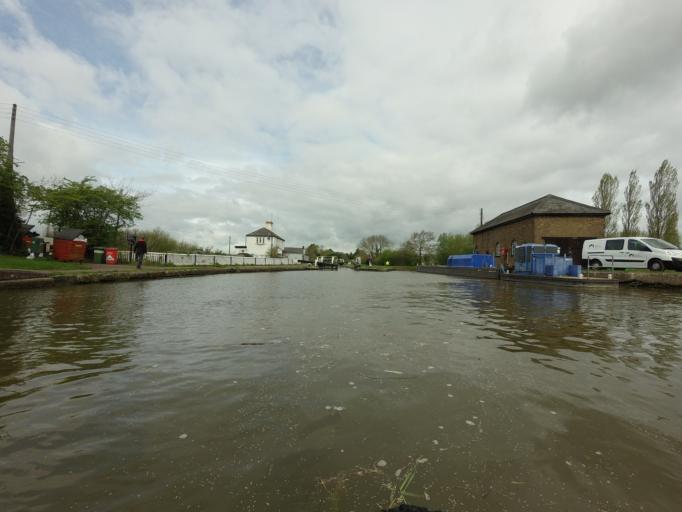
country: GB
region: England
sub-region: Milton Keynes
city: Water Eaton
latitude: 51.9466
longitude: -0.7039
